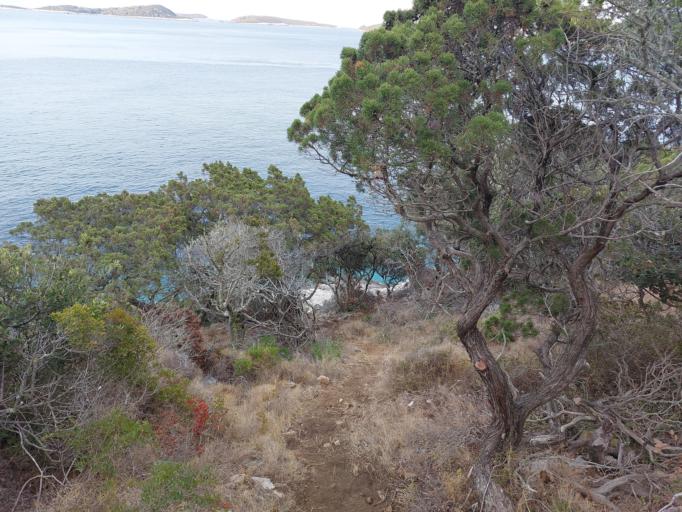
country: HR
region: Dubrovacko-Neretvanska
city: Smokvica
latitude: 42.7610
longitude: 16.9376
